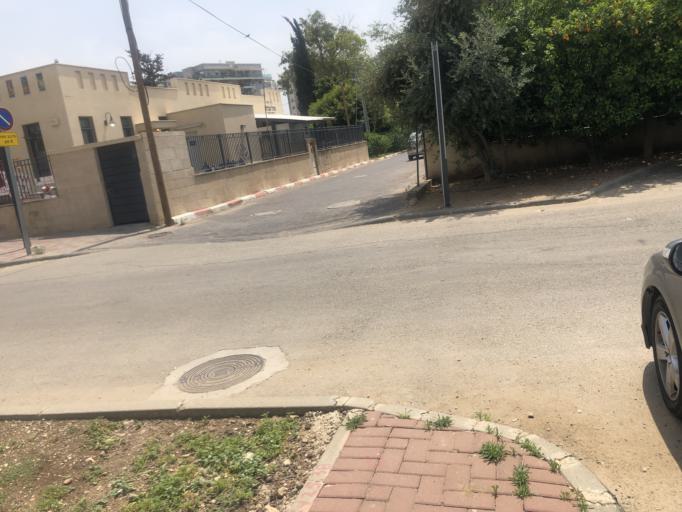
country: IL
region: Central District
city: Rosh Ha'Ayin
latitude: 32.0996
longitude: 34.9398
